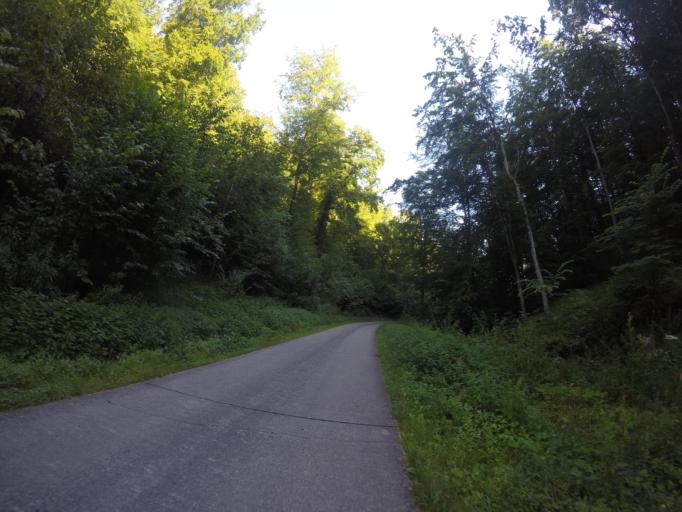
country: DE
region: Baden-Wuerttemberg
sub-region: Tuebingen Region
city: Schelklingen
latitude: 48.3879
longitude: 9.7318
